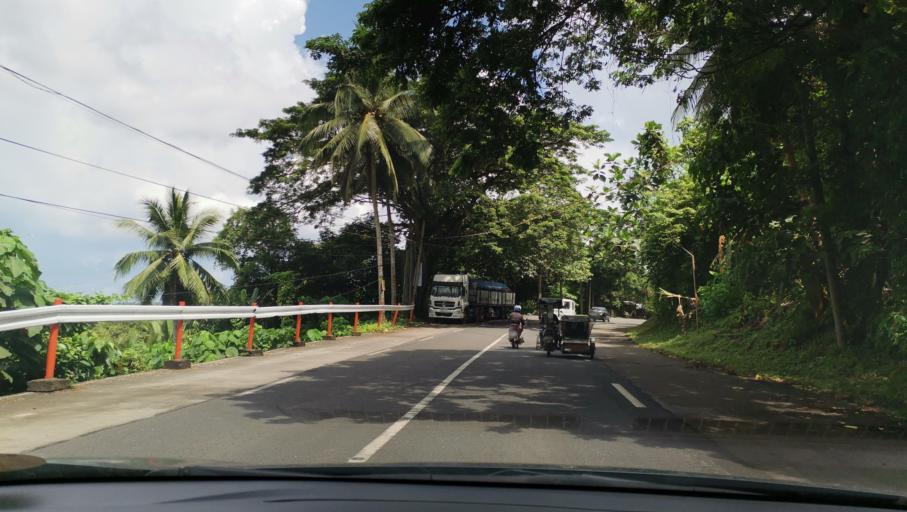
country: PH
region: Calabarzon
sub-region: Province of Quezon
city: Rizal
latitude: 13.9486
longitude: 122.2885
